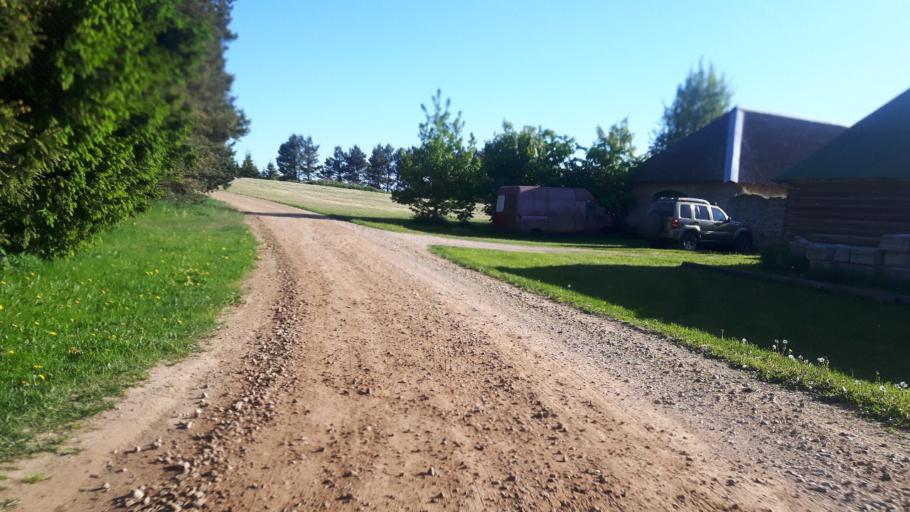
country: EE
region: Ida-Virumaa
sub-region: Puessi linn
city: Pussi
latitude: 59.4259
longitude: 27.0795
